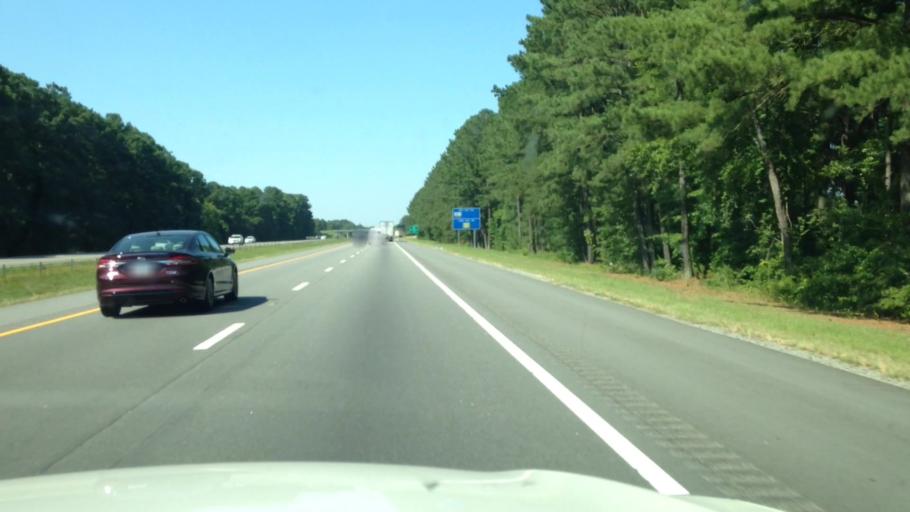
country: US
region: North Carolina
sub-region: Nash County
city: Red Oak
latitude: 36.1198
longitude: -77.7996
